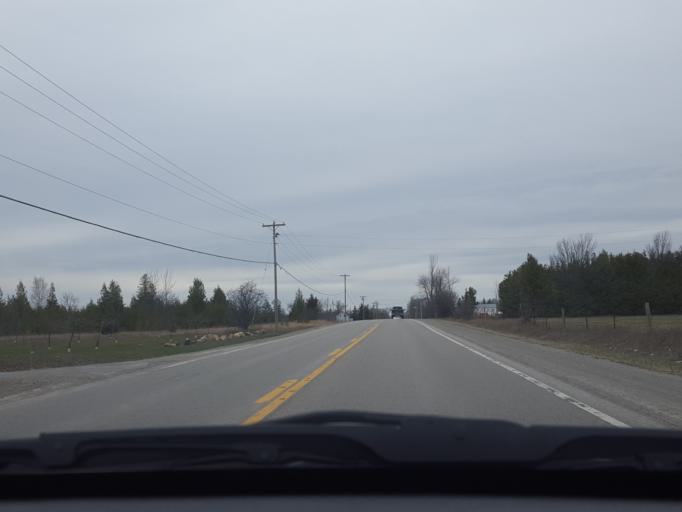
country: CA
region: Ontario
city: Uxbridge
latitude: 44.3257
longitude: -79.1837
